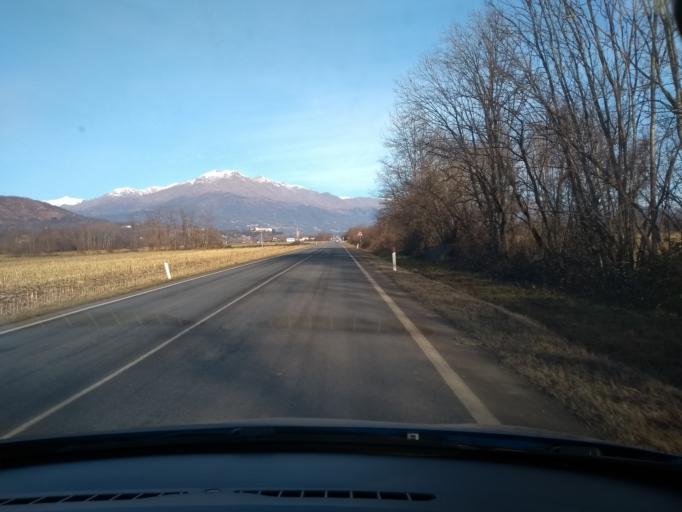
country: IT
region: Piedmont
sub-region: Provincia di Torino
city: Busano
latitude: 45.3418
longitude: 7.6556
